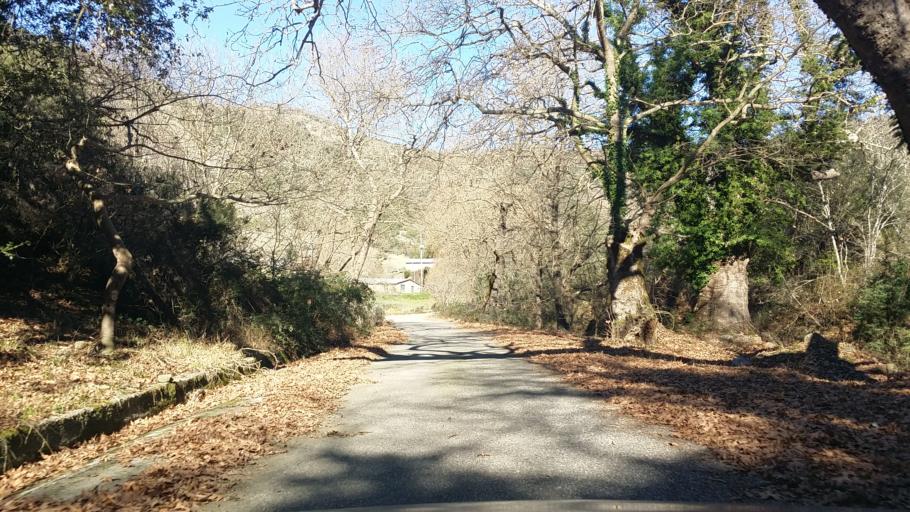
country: GR
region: West Greece
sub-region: Nomos Aitolias kai Akarnanias
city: Krikellos
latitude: 39.0122
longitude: 21.2385
